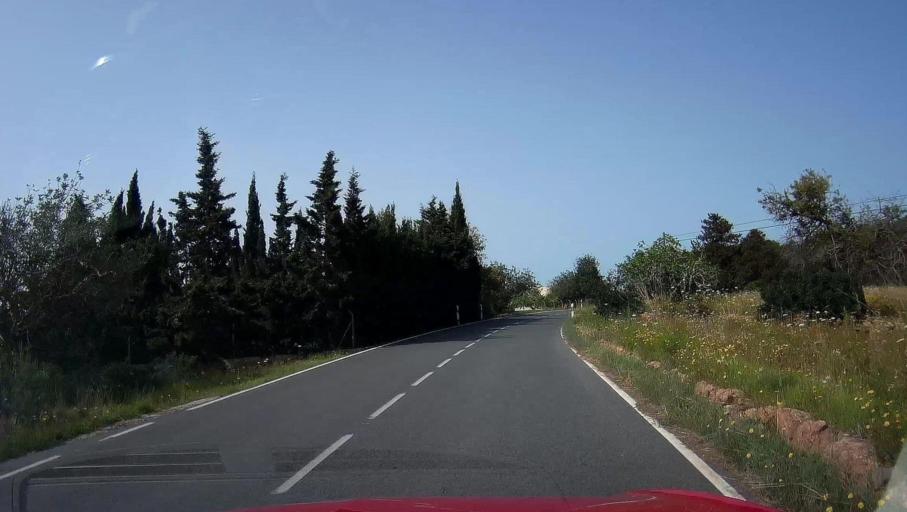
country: ES
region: Balearic Islands
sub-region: Illes Balears
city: Sant Joan de Labritja
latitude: 39.0549
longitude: 1.5804
